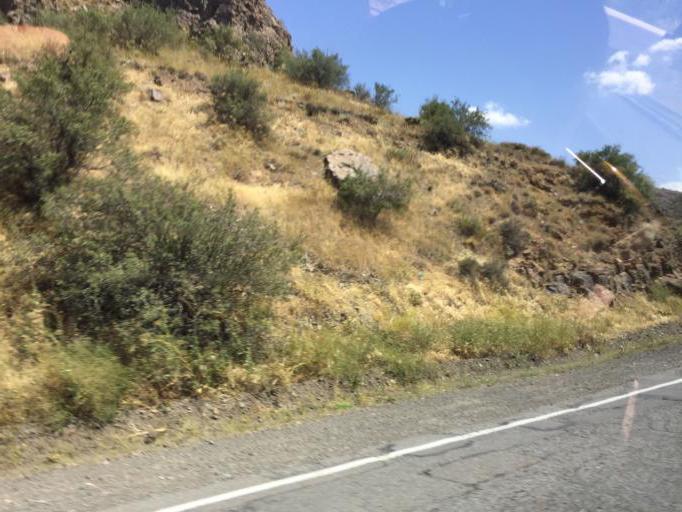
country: AM
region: Vayots' Dzori Marz
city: Jermuk
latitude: 39.7157
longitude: 45.6241
